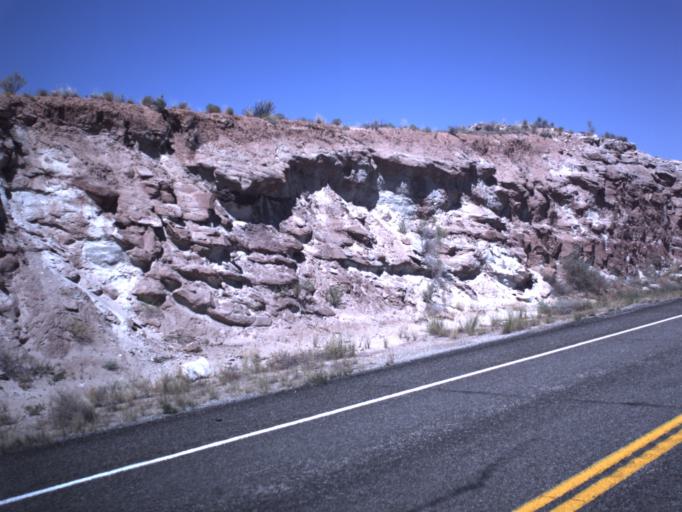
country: US
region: Utah
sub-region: Carbon County
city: East Carbon City
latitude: 38.9069
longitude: -110.3682
